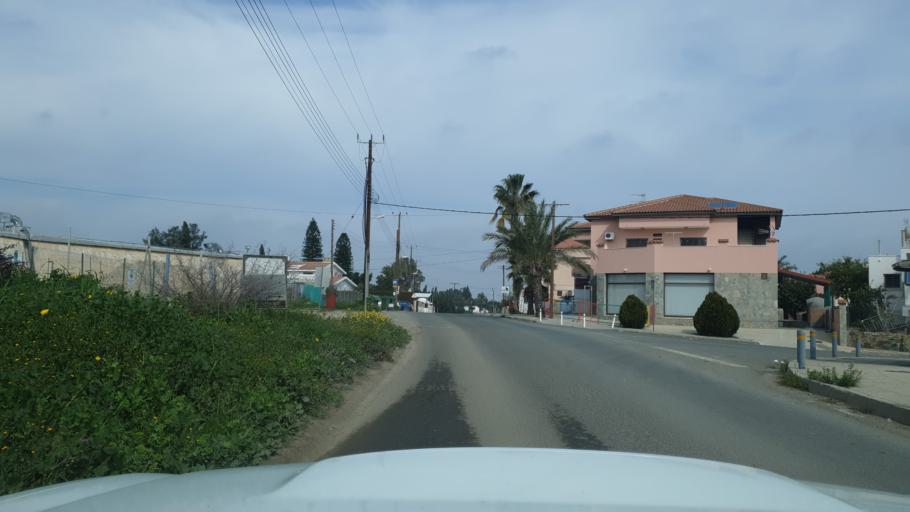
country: CY
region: Lefkosia
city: Tseri
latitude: 35.1215
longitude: 33.3445
